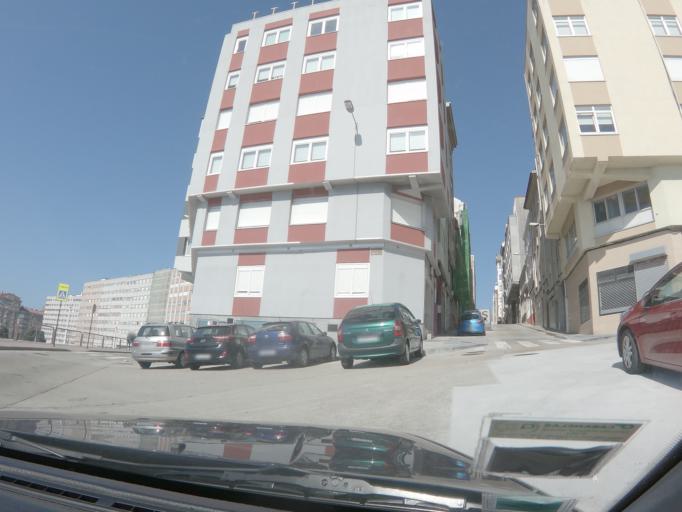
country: ES
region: Galicia
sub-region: Provincia da Coruna
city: A Coruna
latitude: 43.3782
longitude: -8.4073
